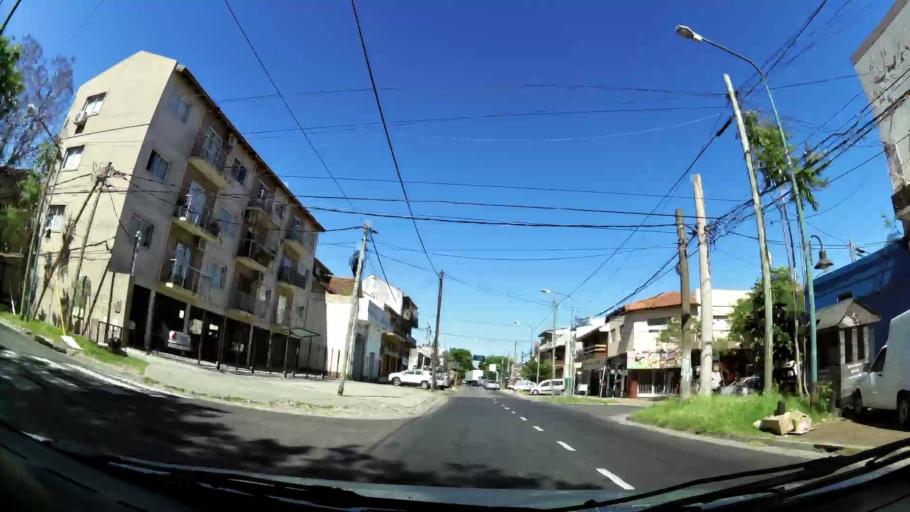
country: AR
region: Buenos Aires
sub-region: Partido de Vicente Lopez
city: Olivos
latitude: -34.5217
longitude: -58.5214
